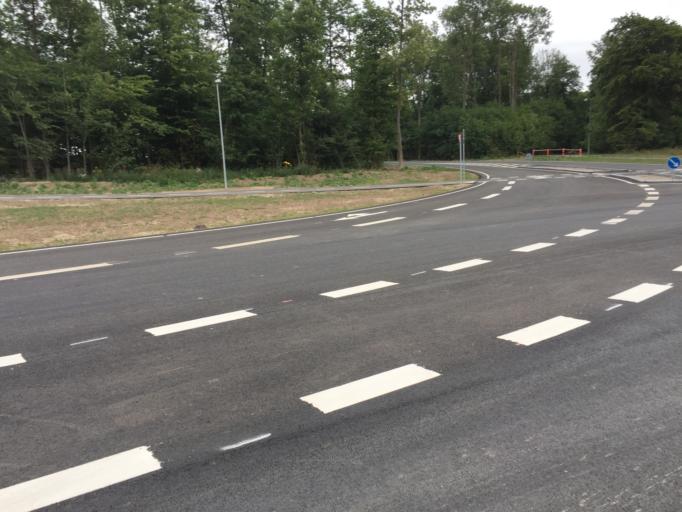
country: DK
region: South Denmark
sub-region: Odense Kommune
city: Hojby
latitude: 55.3563
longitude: 10.4258
